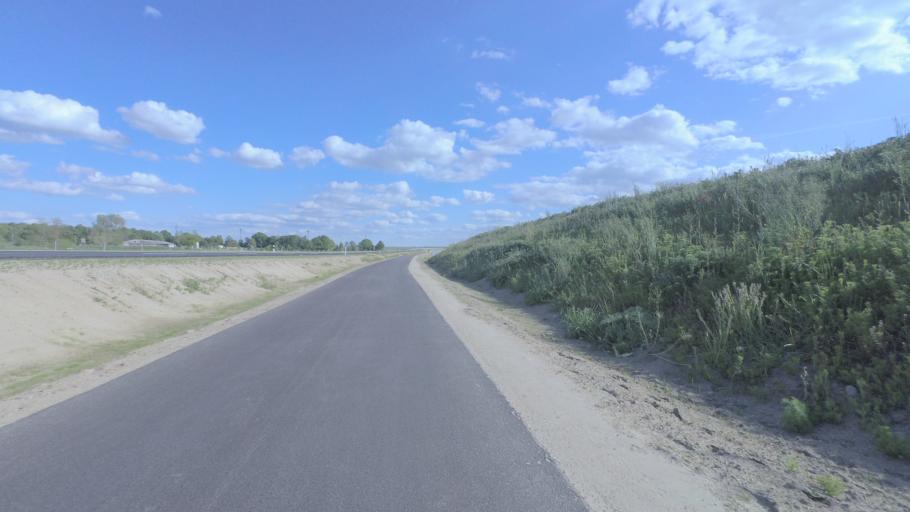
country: DE
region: Brandenburg
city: Stahnsdorf
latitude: 52.3758
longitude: 13.2366
